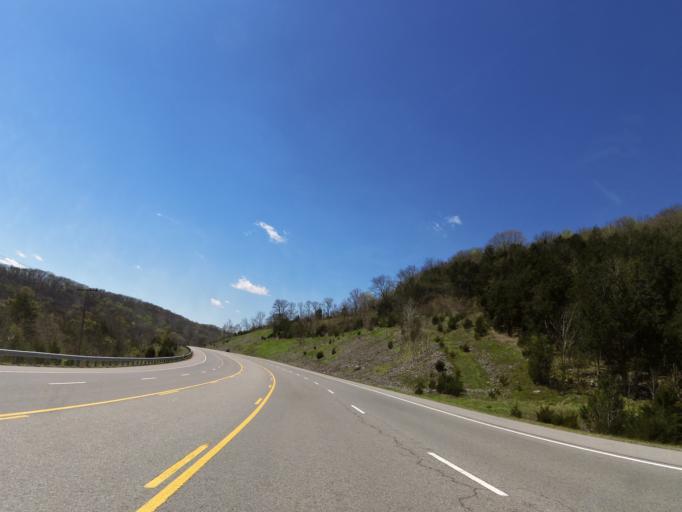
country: US
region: Tennessee
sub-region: DeKalb County
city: Smithville
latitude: 36.0016
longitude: -85.9081
